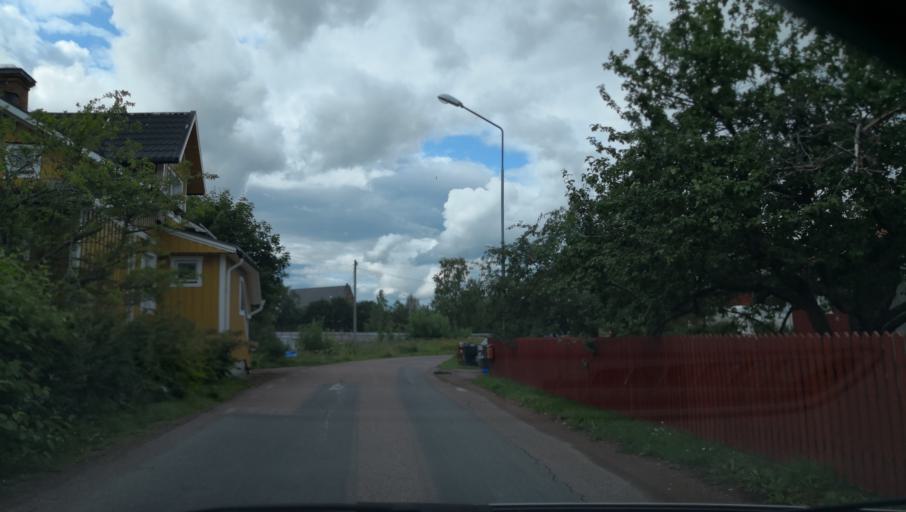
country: SE
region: Dalarna
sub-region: Borlange Kommun
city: Ornas
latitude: 60.4624
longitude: 15.5735
